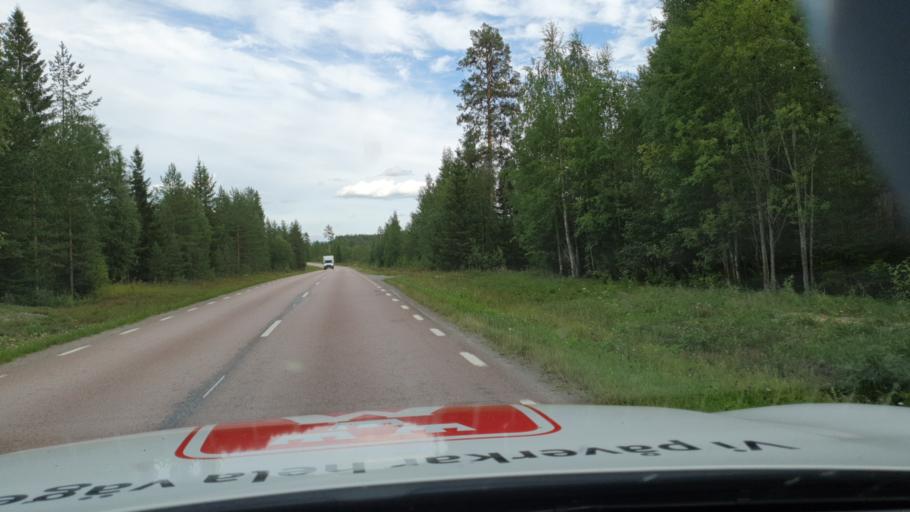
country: SE
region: Vaesternorrland
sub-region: Solleftea Kommun
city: As
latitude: 63.5791
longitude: 16.3557
